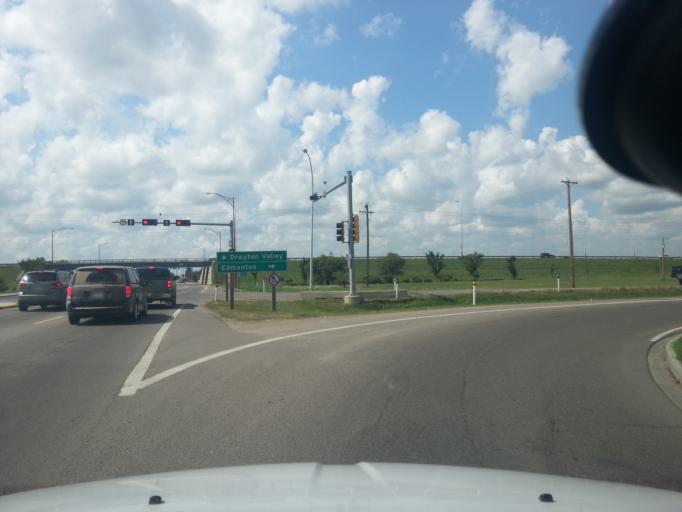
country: CA
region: Alberta
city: Leduc
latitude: 53.2649
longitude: -113.5613
